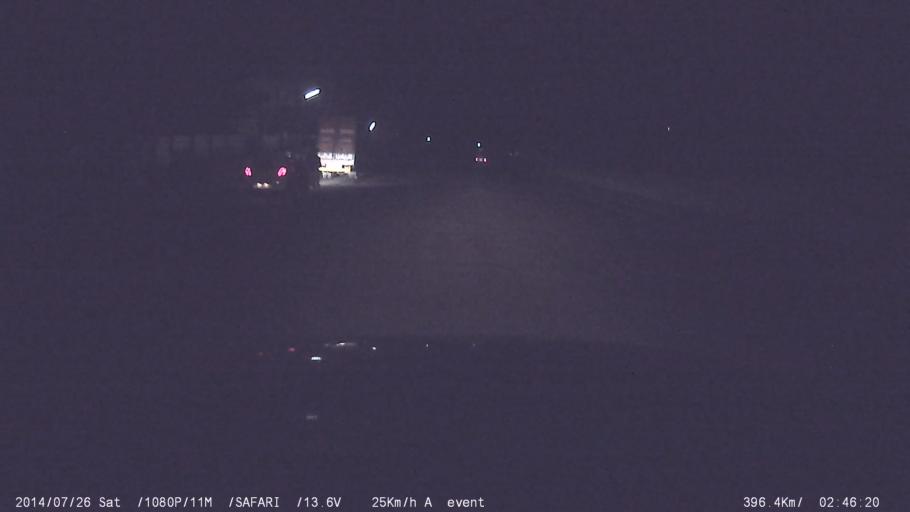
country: IN
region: Kerala
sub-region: Palakkad district
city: Palakkad
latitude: 10.7687
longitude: 76.6791
